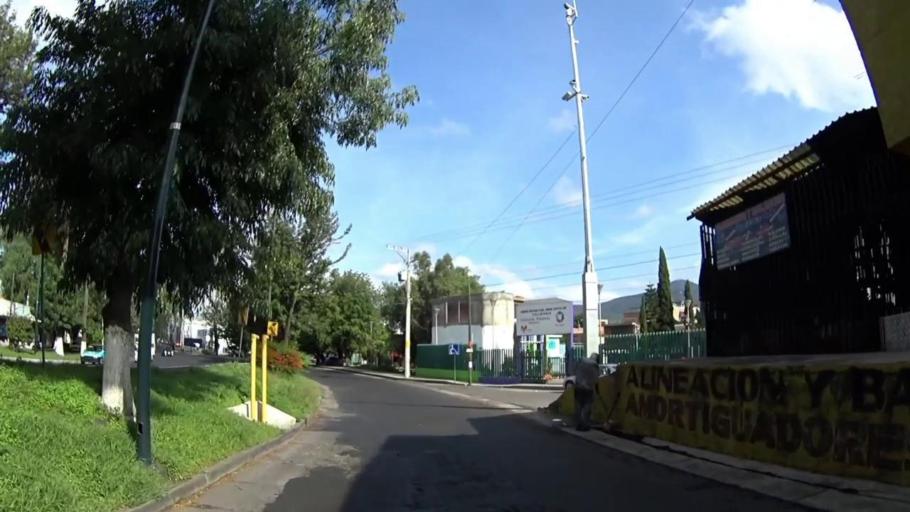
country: MX
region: Michoacan
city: Morelia
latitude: 19.7055
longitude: -101.2193
